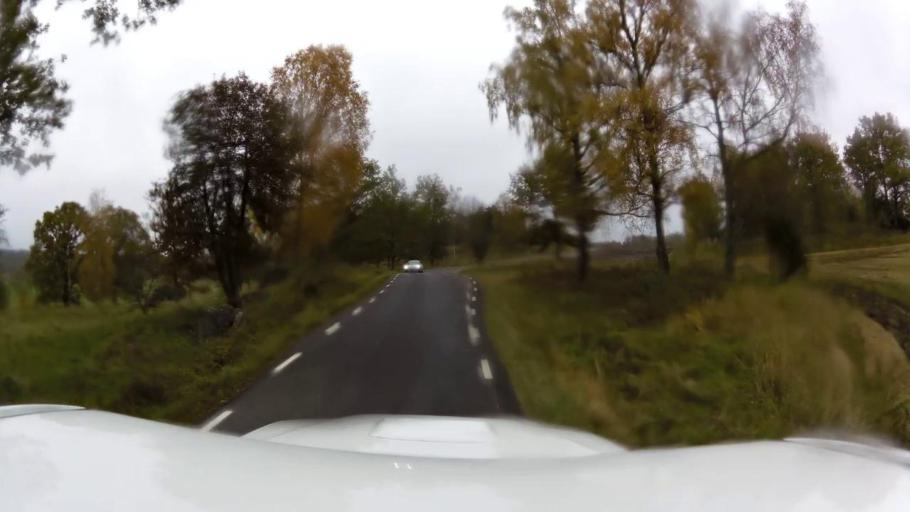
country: SE
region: OEstergoetland
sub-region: Linkopings Kommun
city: Linghem
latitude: 58.3510
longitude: 15.8796
